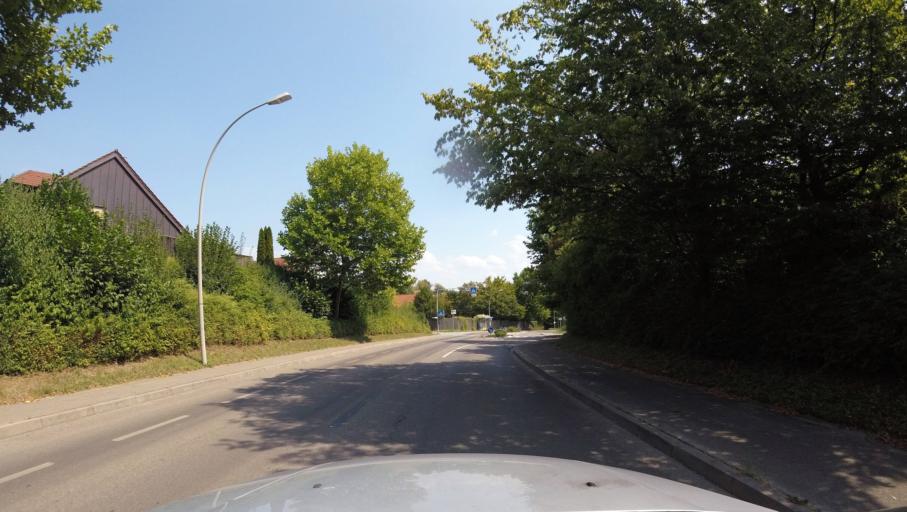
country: DE
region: Baden-Wuerttemberg
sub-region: Regierungsbezirk Stuttgart
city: Backnang
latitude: 48.9534
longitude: 9.4498
